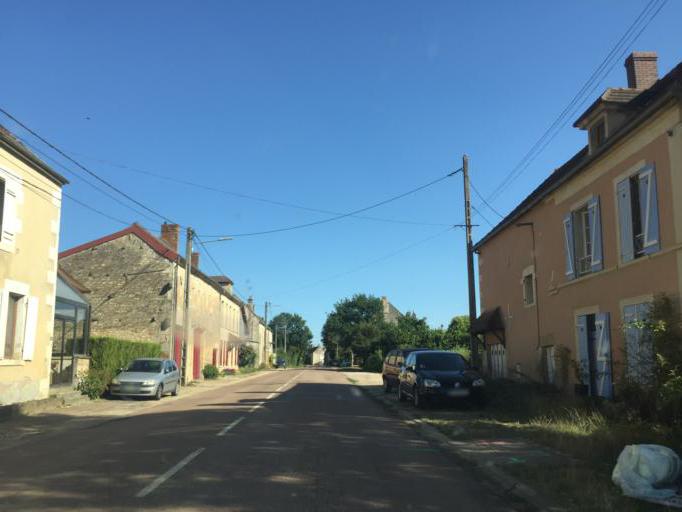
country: FR
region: Bourgogne
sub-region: Departement de la Nievre
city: Clamecy
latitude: 47.4544
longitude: 3.4697
